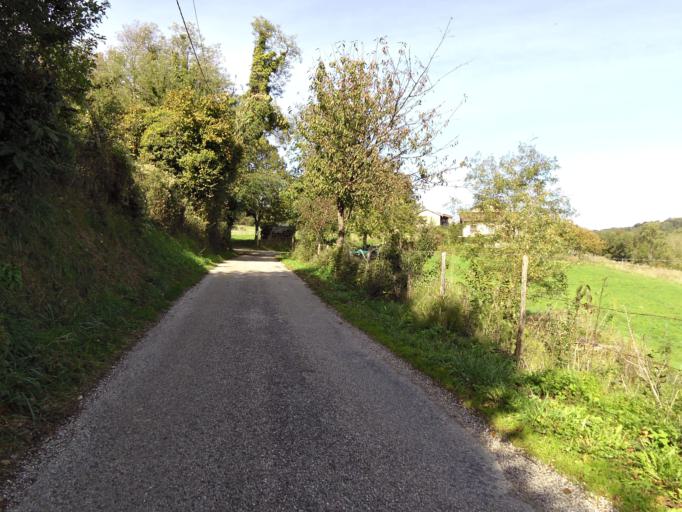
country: FR
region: Rhone-Alpes
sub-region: Departement de l'Ain
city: Perouges
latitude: 45.9102
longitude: 5.1780
